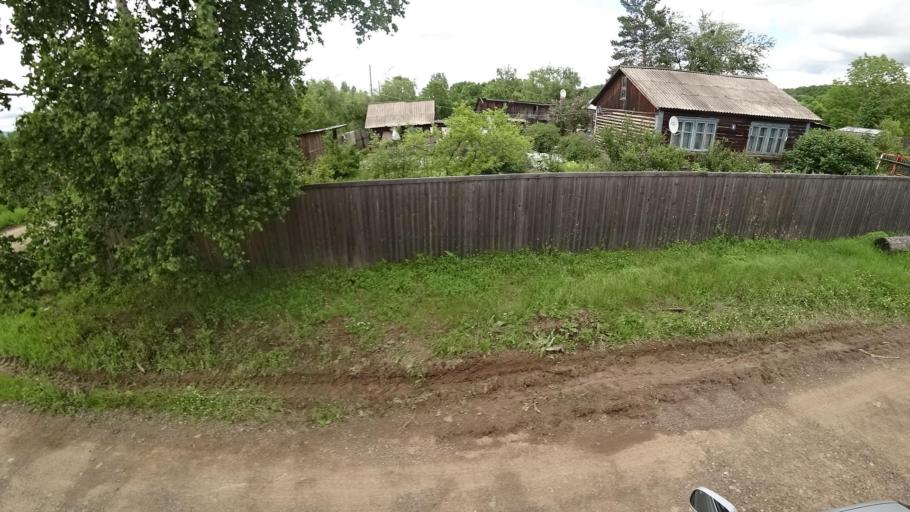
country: RU
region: Khabarovsk Krai
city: Litovko
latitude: 49.3632
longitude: 135.1732
